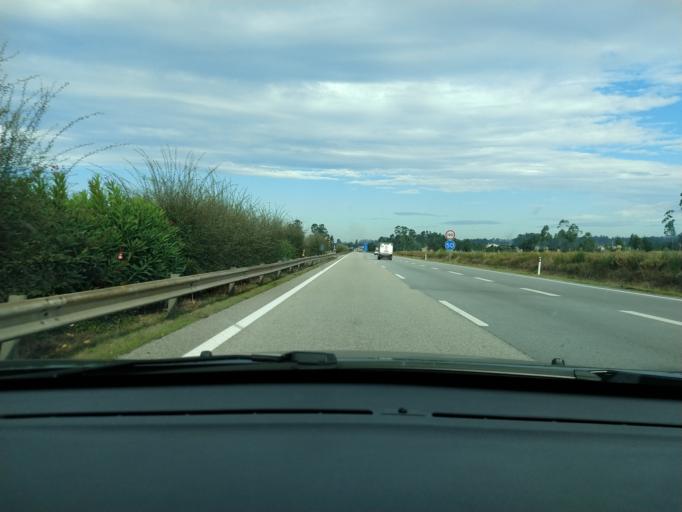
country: PT
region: Aveiro
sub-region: Estarreja
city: Beduido
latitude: 40.7564
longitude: -8.5365
